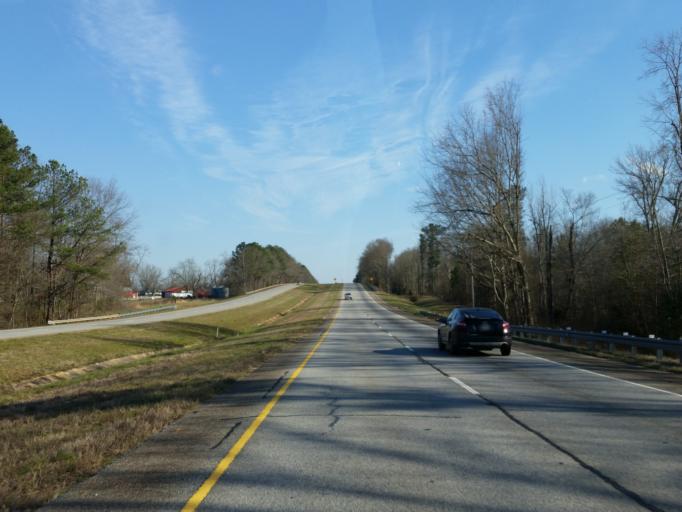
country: US
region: Georgia
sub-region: Lamar County
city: Barnesville
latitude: 33.1111
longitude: -84.2021
